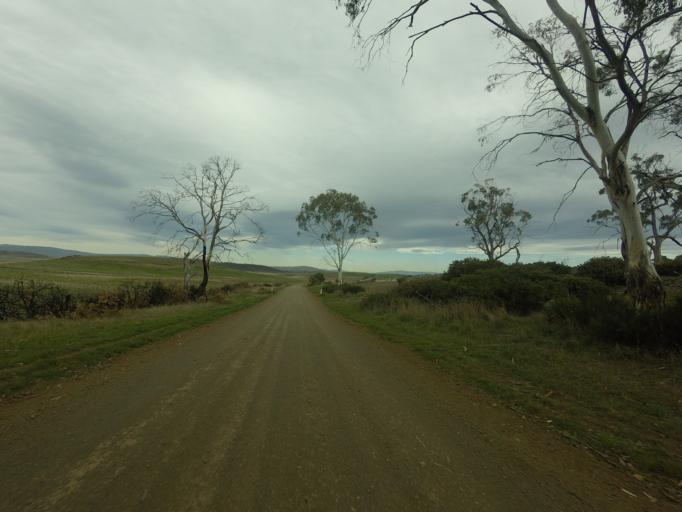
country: AU
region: Tasmania
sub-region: Derwent Valley
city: New Norfolk
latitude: -42.3899
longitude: 146.9773
